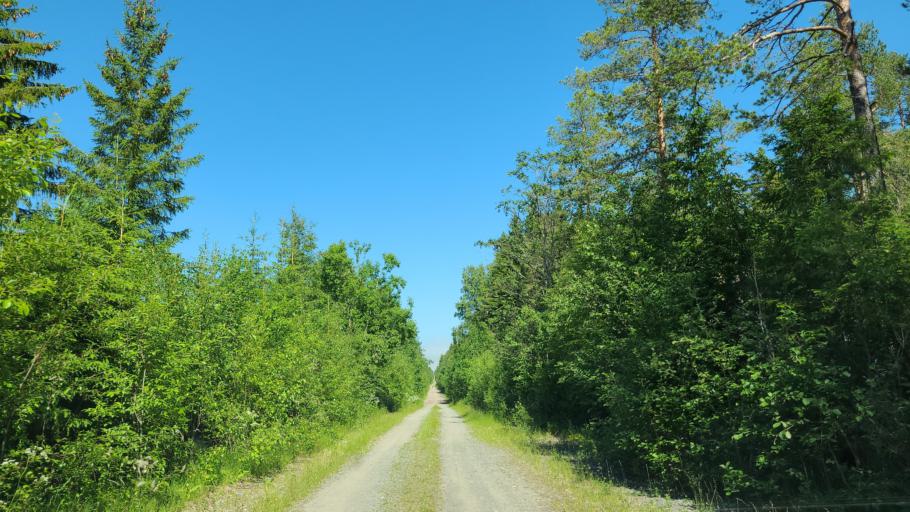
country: SE
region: Vaesternorrland
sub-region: OErnskoeldsviks Kommun
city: Husum
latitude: 63.4208
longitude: 19.2233
